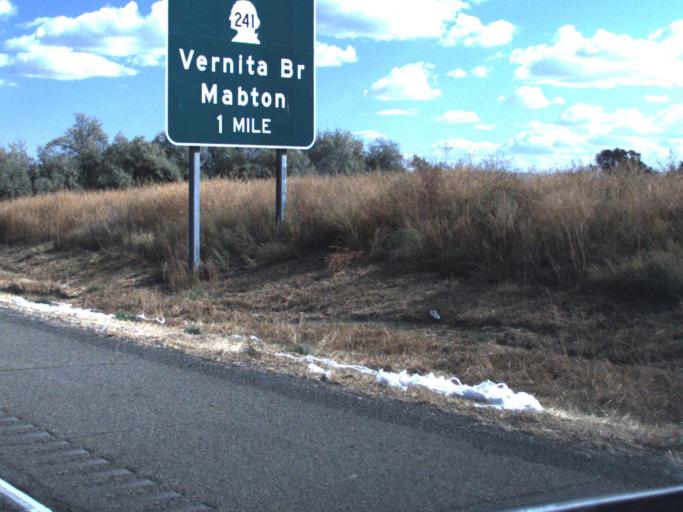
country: US
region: Washington
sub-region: Yakima County
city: Sunnyside
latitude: 46.3059
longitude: -120.0052
